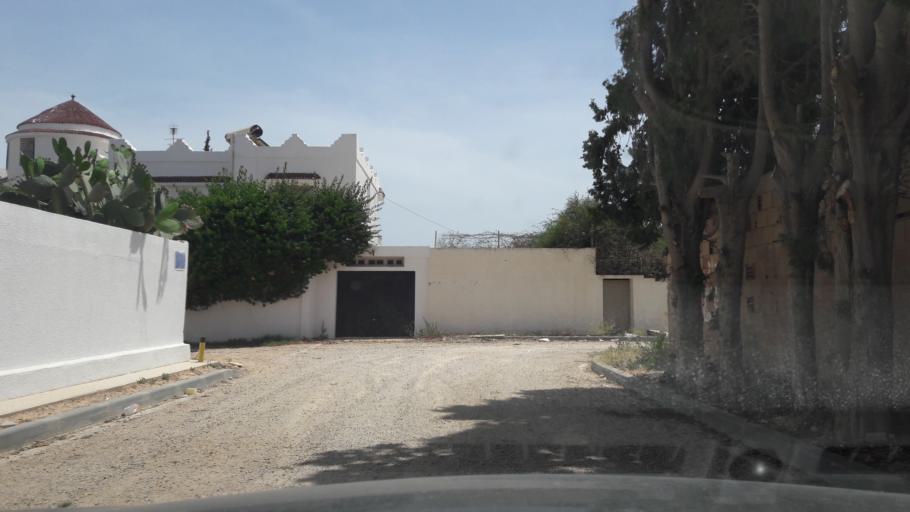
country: TN
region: Safaqis
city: Sfax
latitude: 34.7753
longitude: 10.7542
